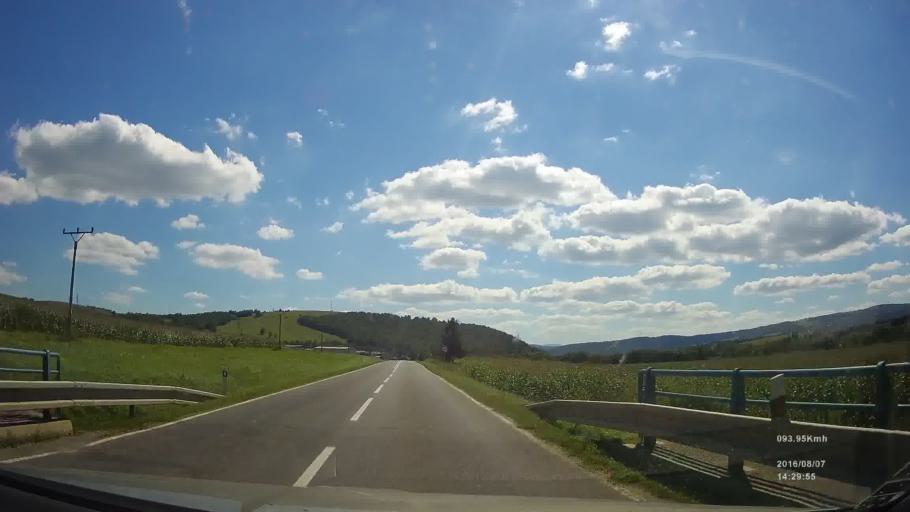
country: SK
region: Presovsky
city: Stropkov
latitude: 49.2380
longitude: 21.6759
